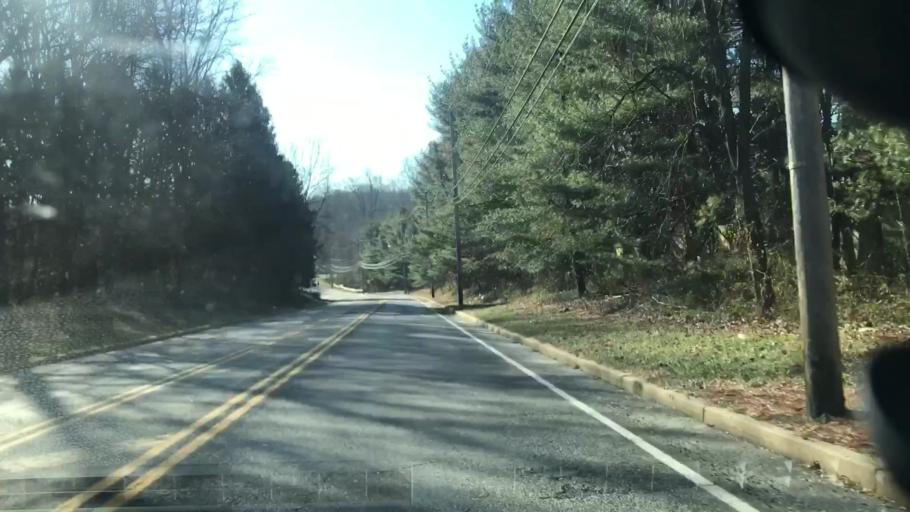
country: US
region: New Jersey
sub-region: Monmouth County
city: Keansburg
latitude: 40.3866
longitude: -74.1454
